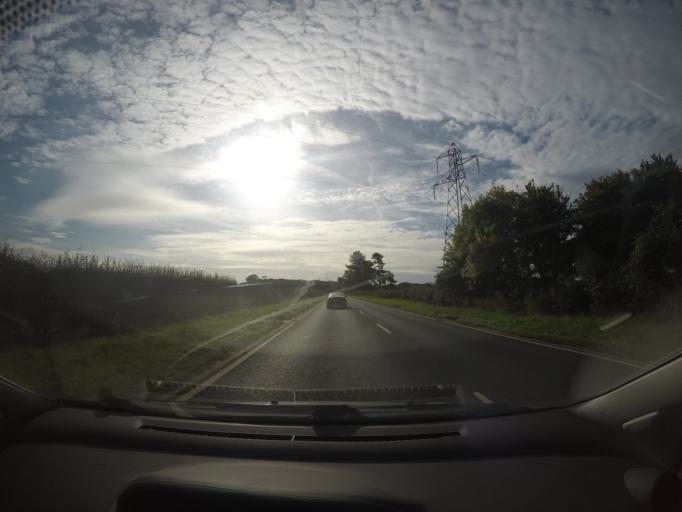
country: GB
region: England
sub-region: City of York
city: Deighton
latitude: 53.9163
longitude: -1.0561
